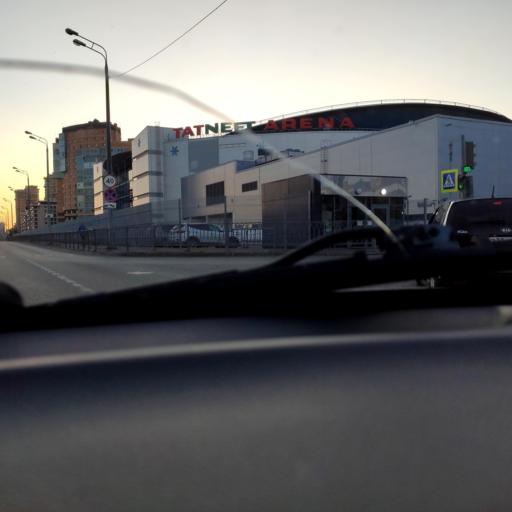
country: RU
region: Tatarstan
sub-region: Gorod Kazan'
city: Kazan
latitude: 55.8152
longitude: 49.1256
